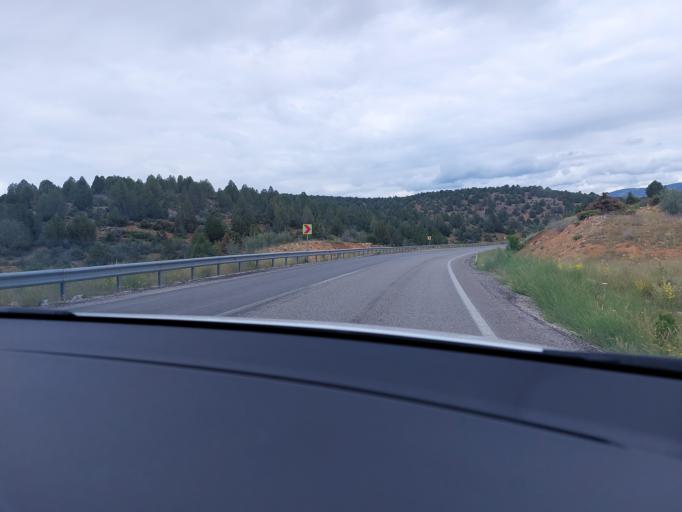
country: TR
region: Konya
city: Doganbey
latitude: 37.8858
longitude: 31.8250
